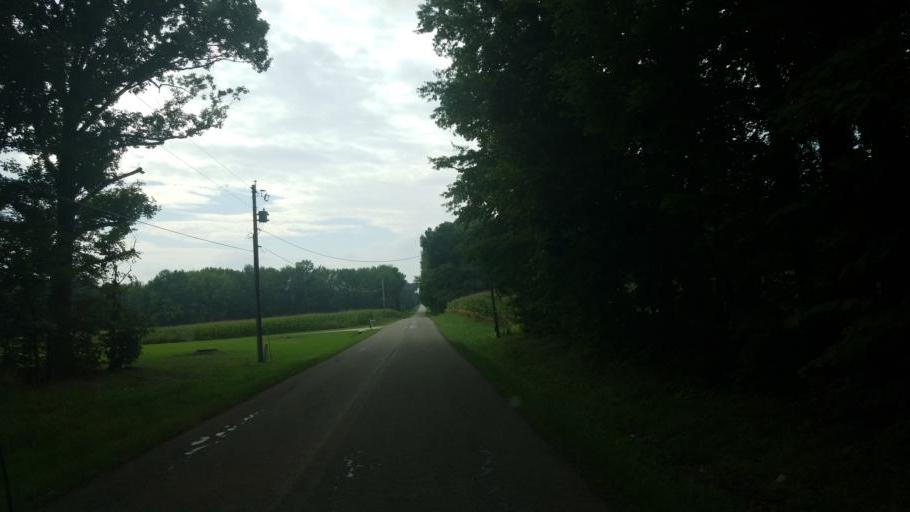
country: US
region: Ohio
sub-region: Wayne County
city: Wooster
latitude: 40.9011
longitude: -81.9625
